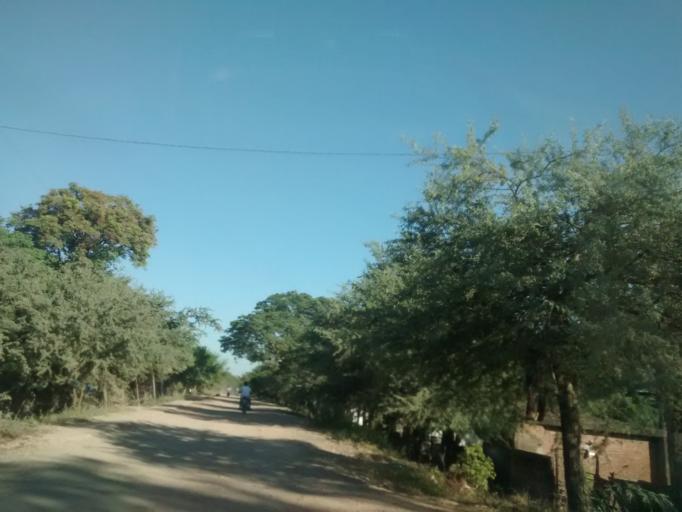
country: AR
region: Chaco
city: Resistencia
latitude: -27.4587
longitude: -58.9610
